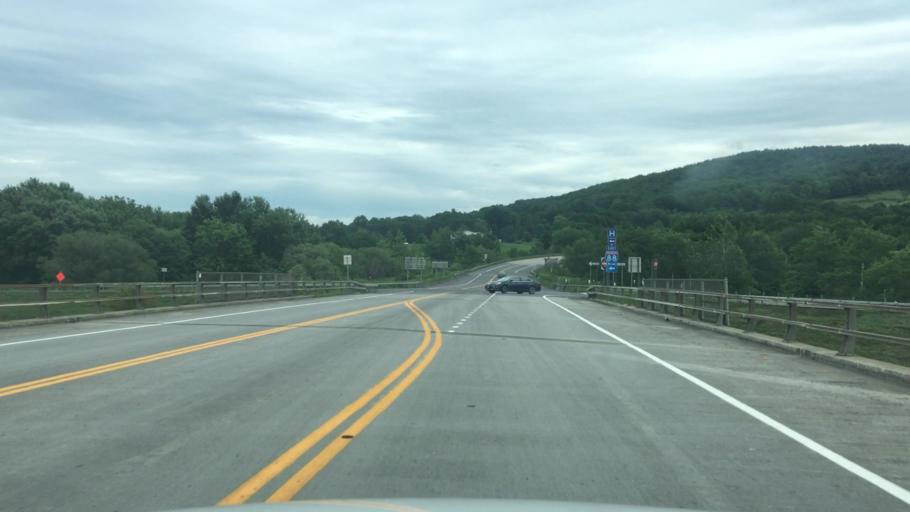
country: US
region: New York
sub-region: Otsego County
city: West End
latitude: 42.4408
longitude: -75.1036
